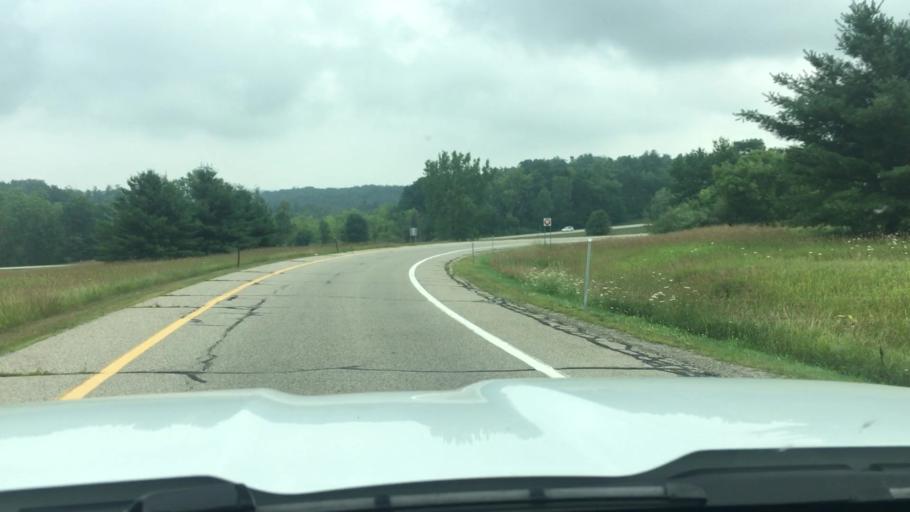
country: US
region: Michigan
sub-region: Lapeer County
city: Lapeer
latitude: 43.0055
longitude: -83.2153
